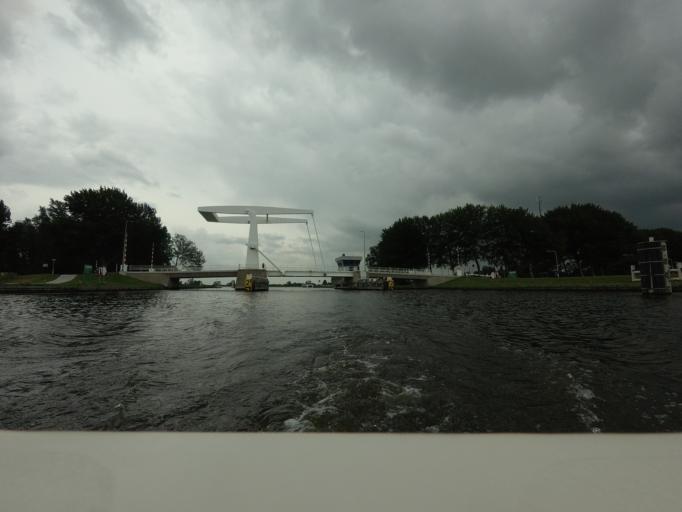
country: NL
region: Friesland
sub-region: Gemeente Smallingerland
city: Oudega
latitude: 53.1053
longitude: 5.9494
